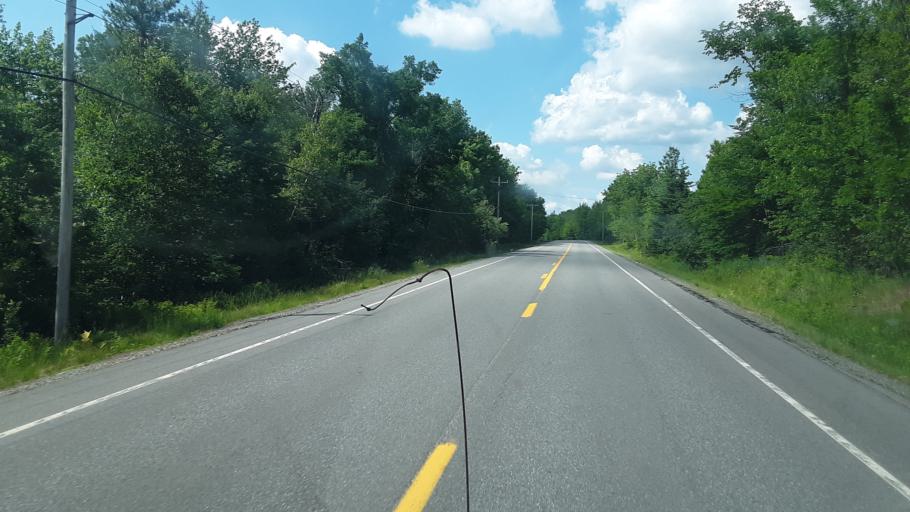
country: US
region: Maine
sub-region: Washington County
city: Machias
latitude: 45.0095
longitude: -67.5541
